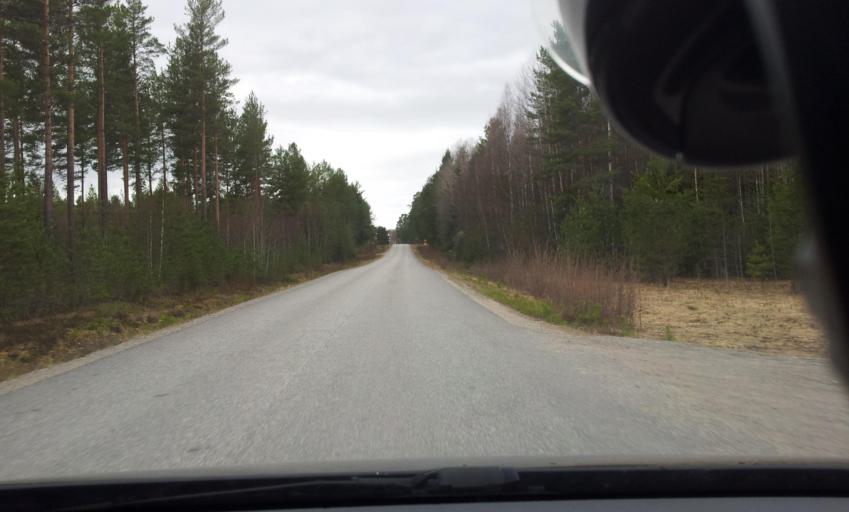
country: SE
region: Gaevleborg
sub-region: Ljusdals Kommun
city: Farila
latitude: 61.8157
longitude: 15.9337
